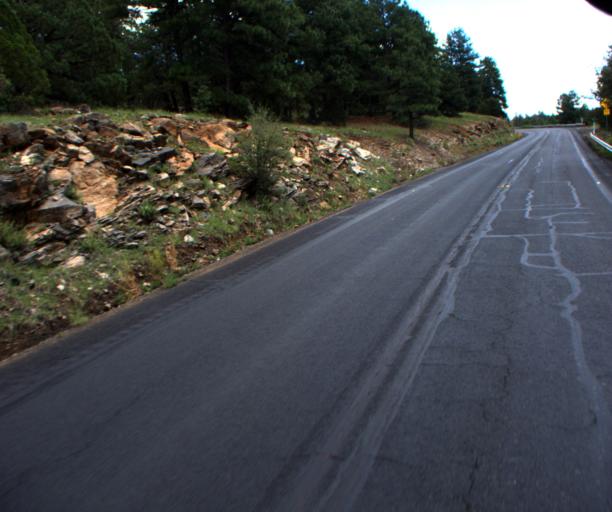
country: US
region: Arizona
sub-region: Gila County
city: Pine
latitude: 34.5162
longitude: -111.4974
